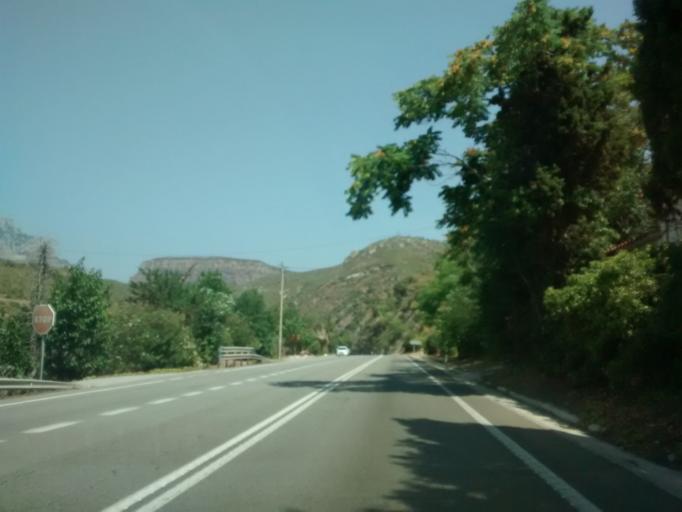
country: ES
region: Catalonia
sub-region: Provincia de Barcelona
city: Olesa de Montserrat
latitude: 41.5641
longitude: 1.8817
